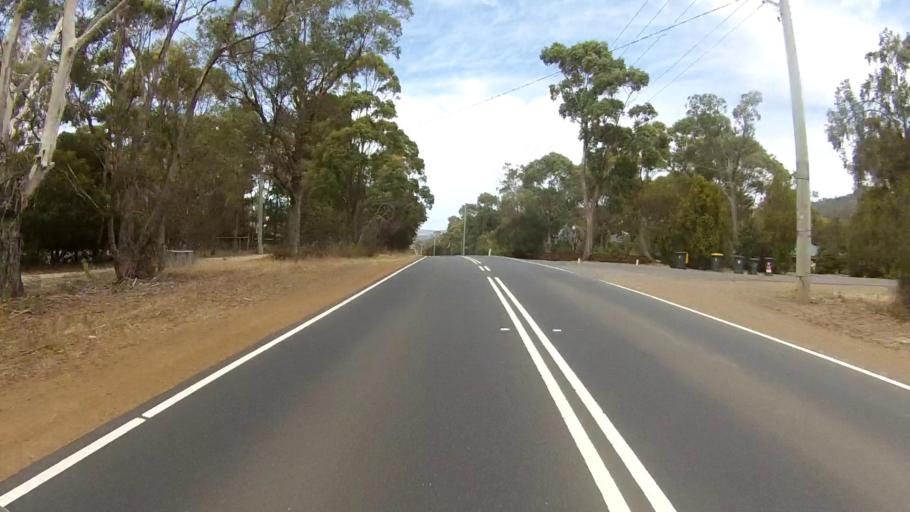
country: AU
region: Tasmania
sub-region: Clarence
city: Acton Park
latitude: -42.8808
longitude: 147.4820
